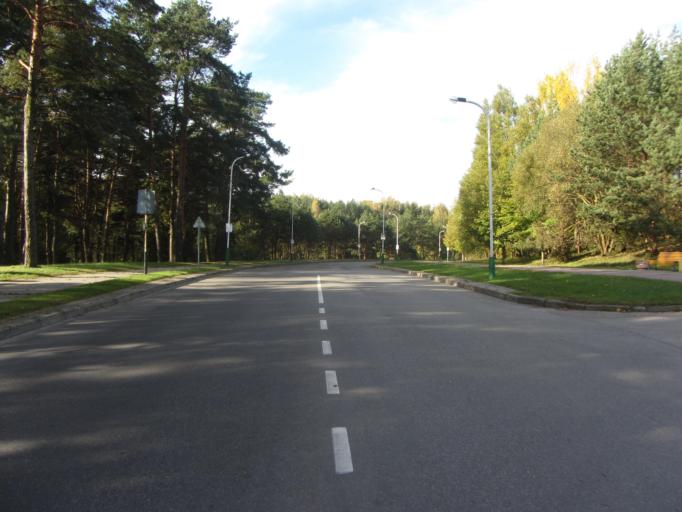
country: LT
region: Vilnius County
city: Elektrenai
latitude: 54.7833
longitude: 24.6798
